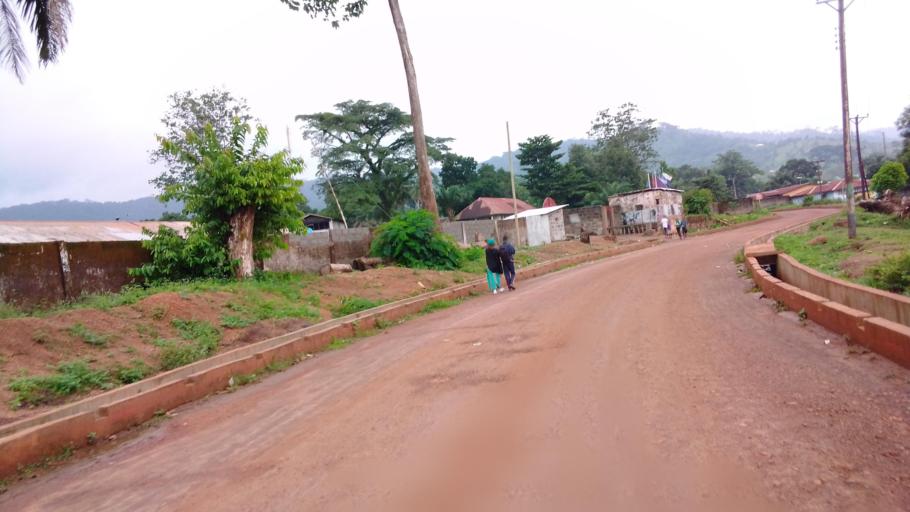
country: SL
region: Eastern Province
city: Kenema
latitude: 7.8848
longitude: -11.1908
